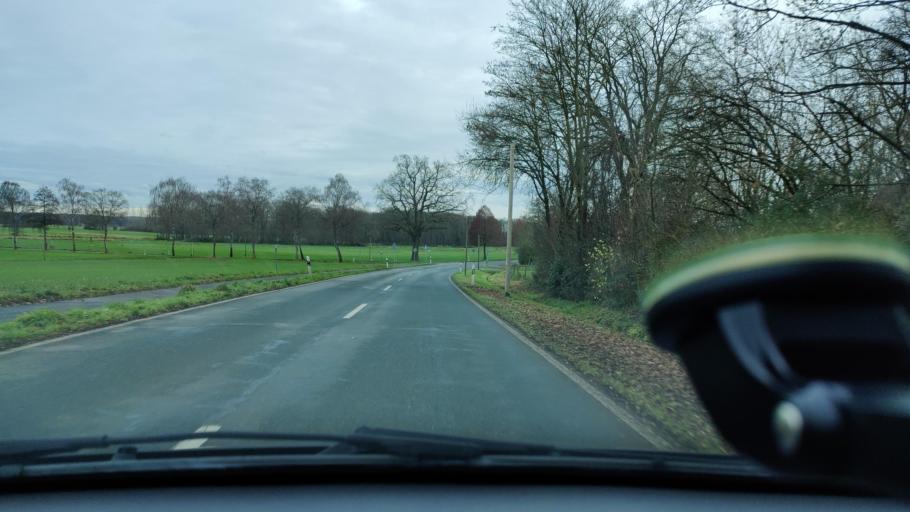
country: DE
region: North Rhine-Westphalia
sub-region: Regierungsbezirk Dusseldorf
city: Xanten
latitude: 51.6241
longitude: 6.4174
